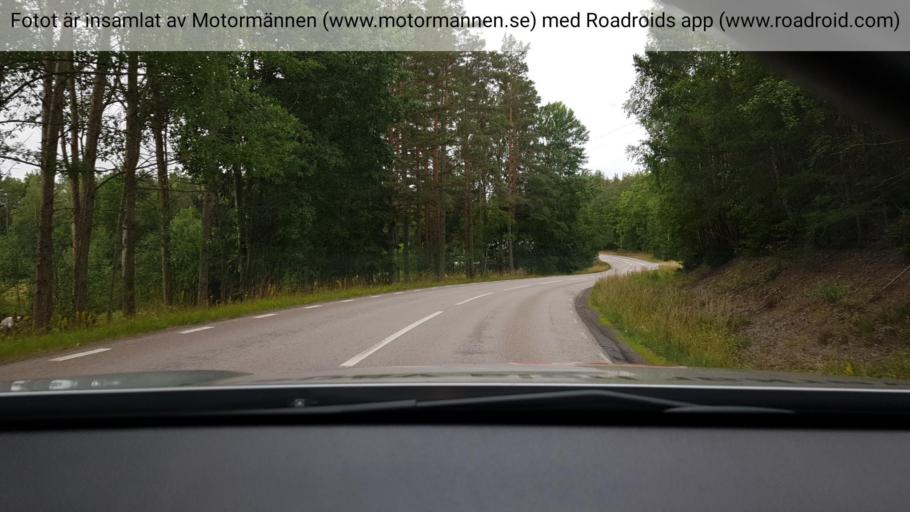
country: SE
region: Soedermanland
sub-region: Strangnas Kommun
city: Mariefred
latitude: 59.1989
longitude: 17.1902
